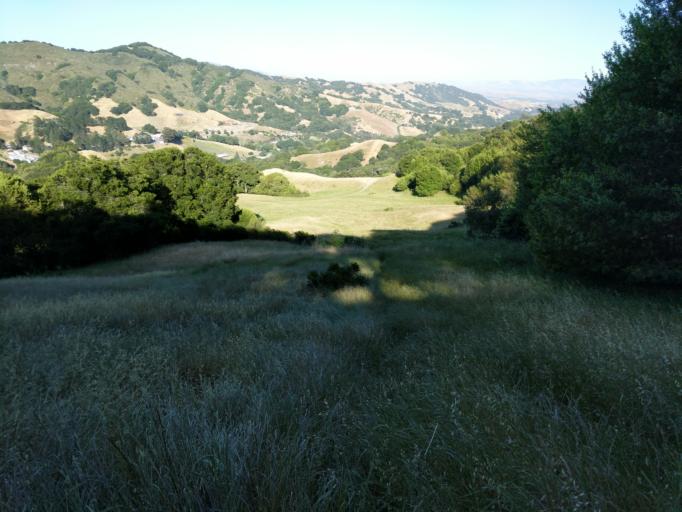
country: US
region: California
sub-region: Contra Costa County
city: Alamo
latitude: 37.8100
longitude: -122.0528
